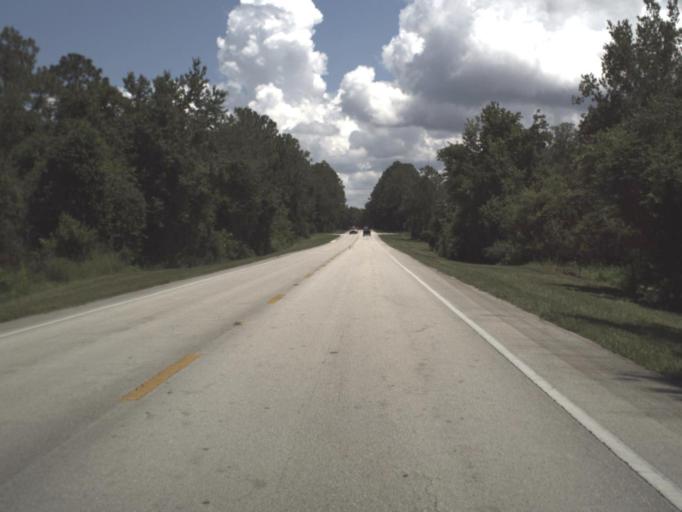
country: US
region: Florida
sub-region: Putnam County
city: Crescent City
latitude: 29.3814
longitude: -81.5088
